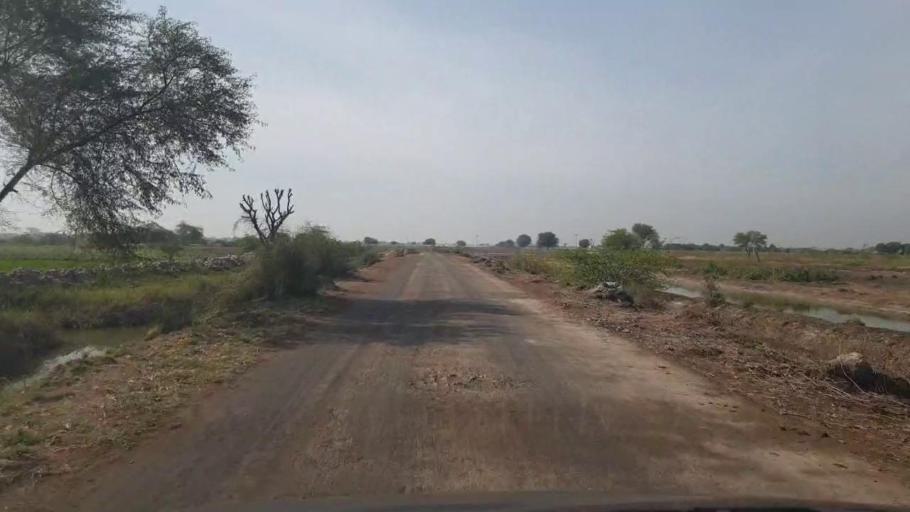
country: PK
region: Sindh
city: Umarkot
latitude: 25.3596
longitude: 69.6811
